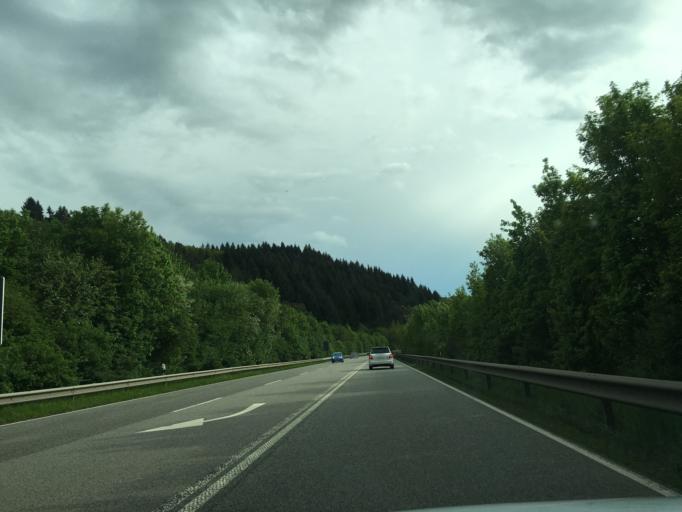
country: DE
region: Rheinland-Pfalz
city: Barenbach
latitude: 49.7584
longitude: 7.4369
